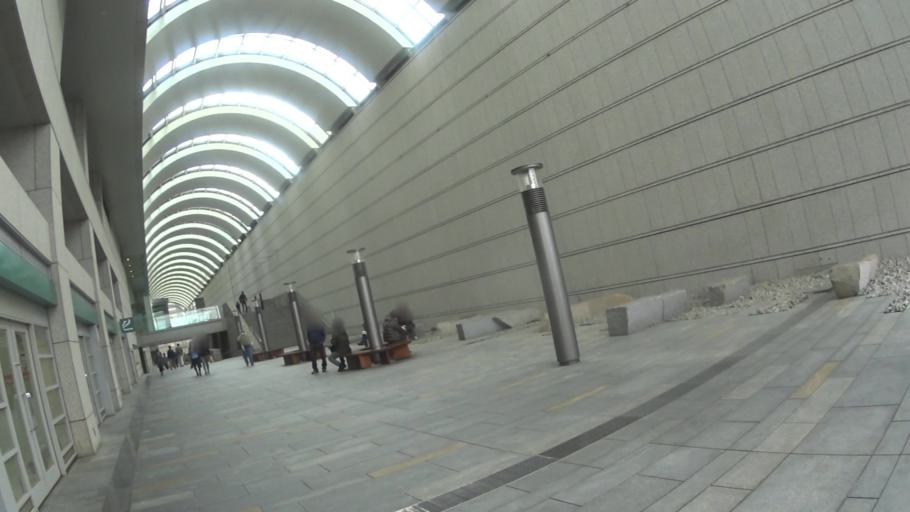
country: JP
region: Tokyo
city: Tokyo
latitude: 35.6841
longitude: 139.6861
